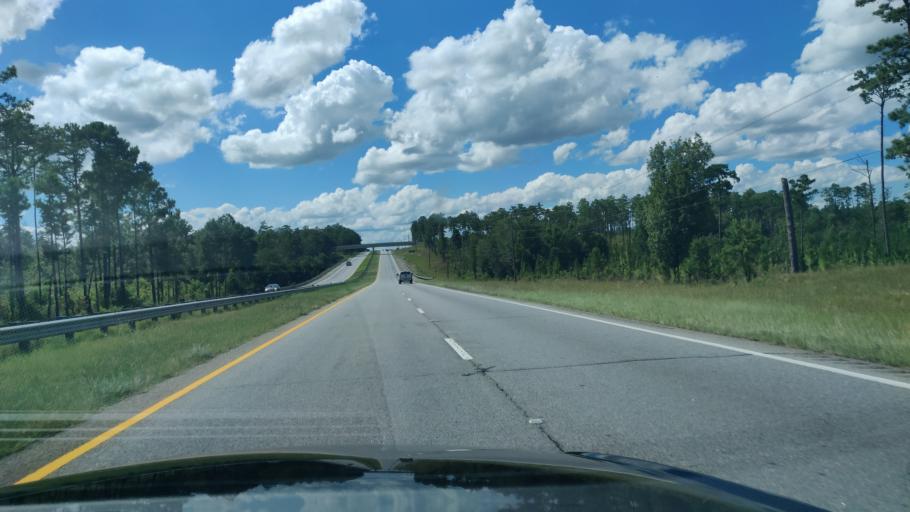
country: US
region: Georgia
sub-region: Chattahoochee County
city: Cusseta
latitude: 32.3595
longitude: -84.8436
